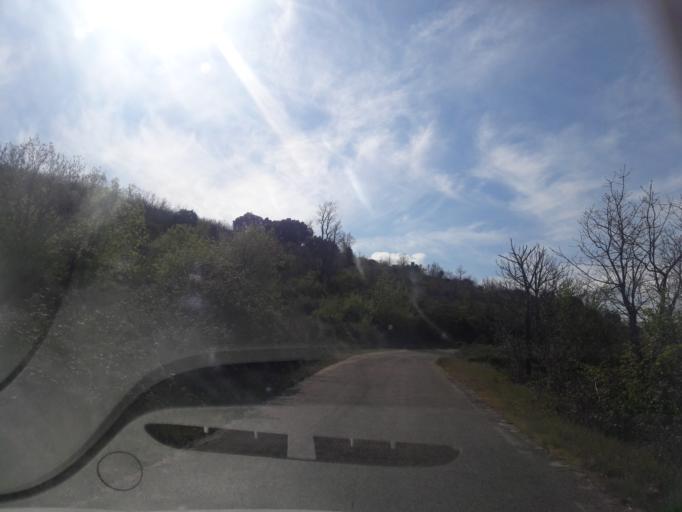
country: ES
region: Castille and Leon
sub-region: Provincia de Salamanca
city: San Esteban de la Sierra
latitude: 40.5089
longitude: -5.8861
